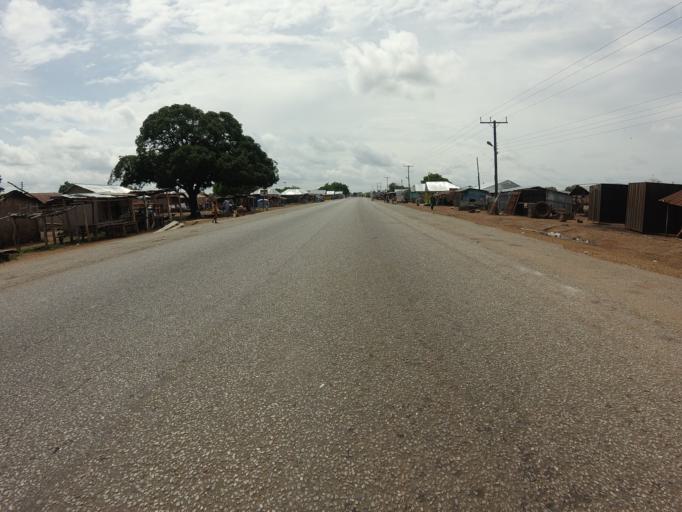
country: GH
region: Brong-Ahafo
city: Kintampo
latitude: 8.4480
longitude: -1.5649
